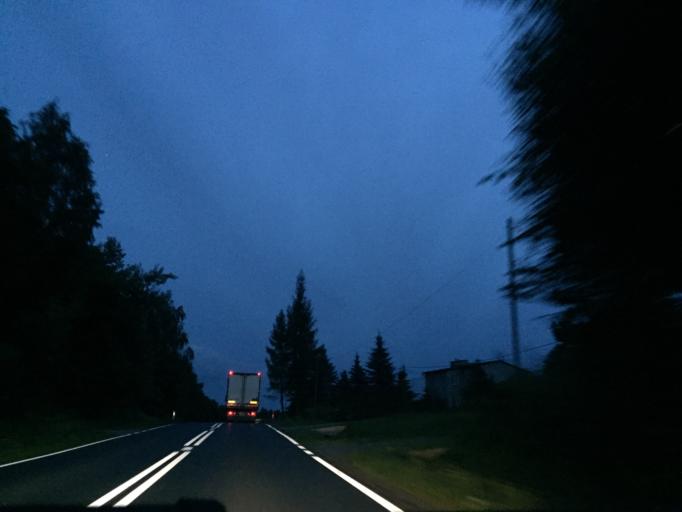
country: PL
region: Lesser Poland Voivodeship
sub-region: Powiat oswiecimski
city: Wlosienica
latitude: 50.0175
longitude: 19.3416
